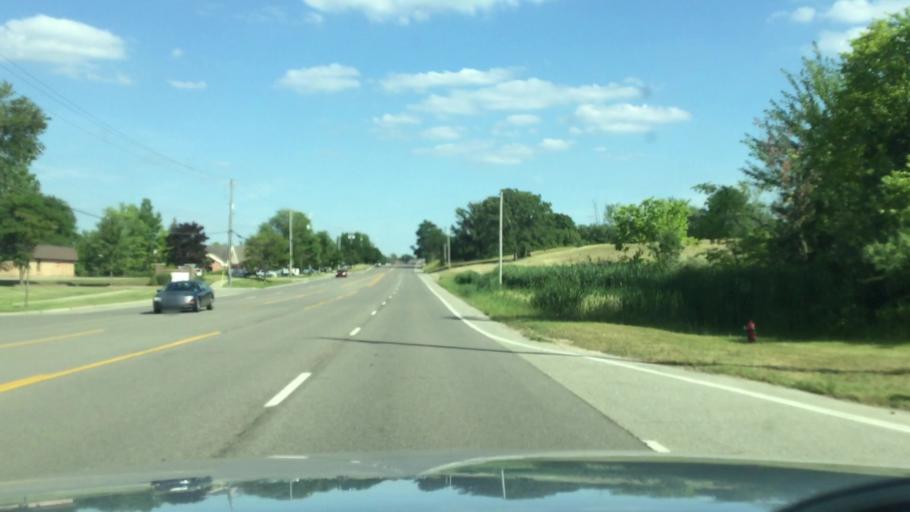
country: US
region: Michigan
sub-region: Genesee County
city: Grand Blanc
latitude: 42.9146
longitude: -83.6123
